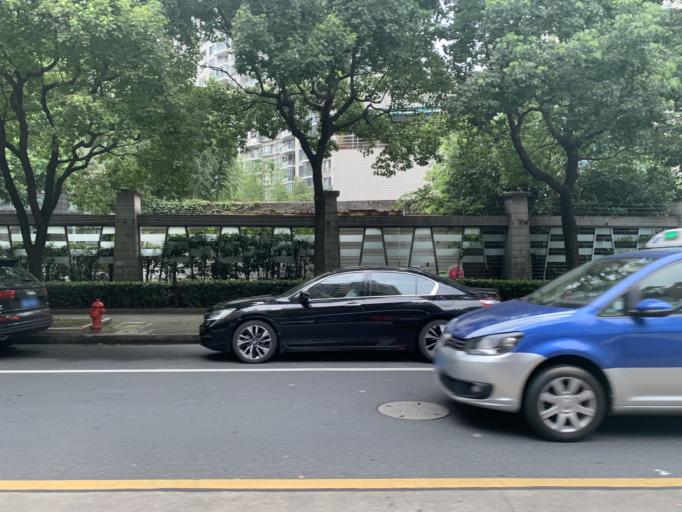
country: CN
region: Shanghai Shi
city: Huamu
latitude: 31.2300
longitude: 121.5608
